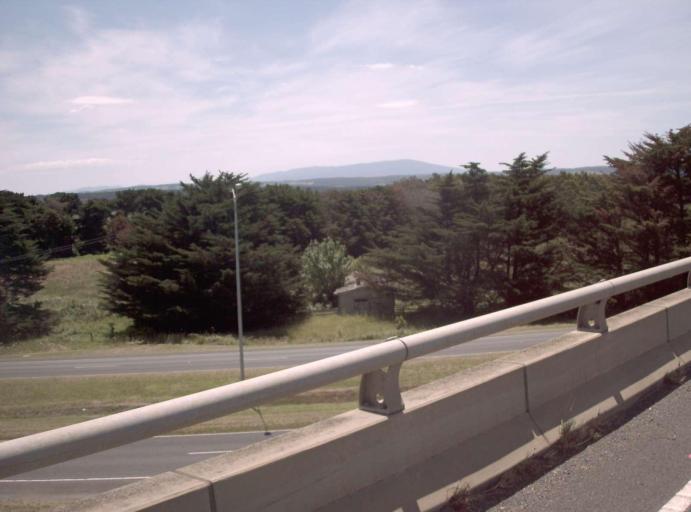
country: AU
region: Victoria
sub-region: Latrobe
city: Morwell
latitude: -38.2303
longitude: 146.4564
